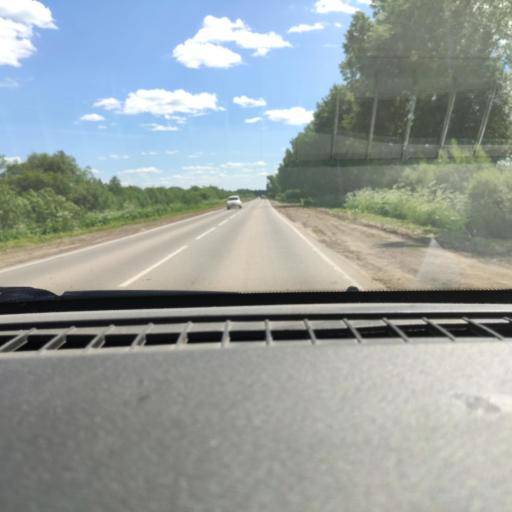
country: RU
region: Perm
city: Chaykovskaya
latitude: 58.1055
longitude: 55.5892
